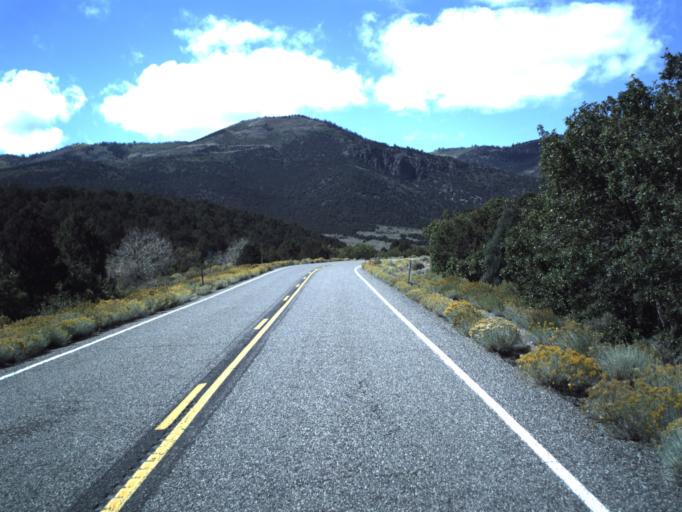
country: US
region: Utah
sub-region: Piute County
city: Junction
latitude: 38.2572
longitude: -112.2848
